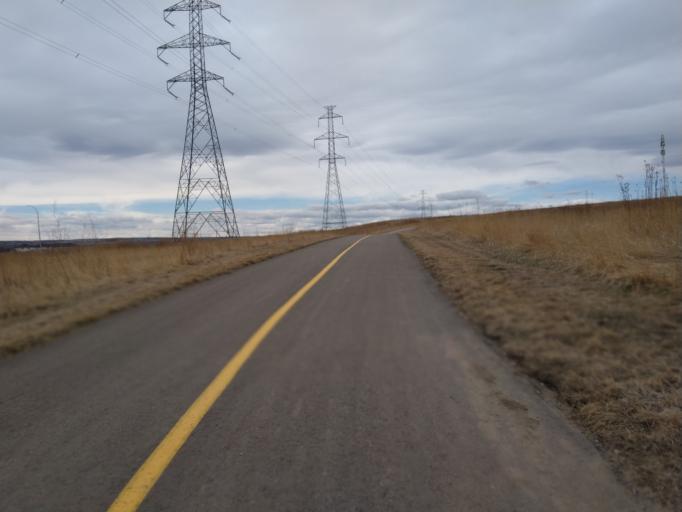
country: CA
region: Alberta
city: Calgary
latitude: 51.1744
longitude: -114.0606
